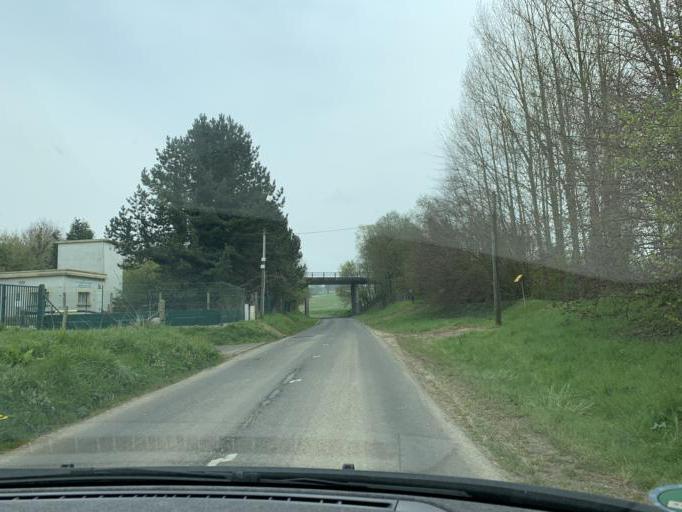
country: FR
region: Haute-Normandie
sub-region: Departement de la Seine-Maritime
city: Saint-Valery-en-Caux
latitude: 49.8539
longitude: 0.7269
